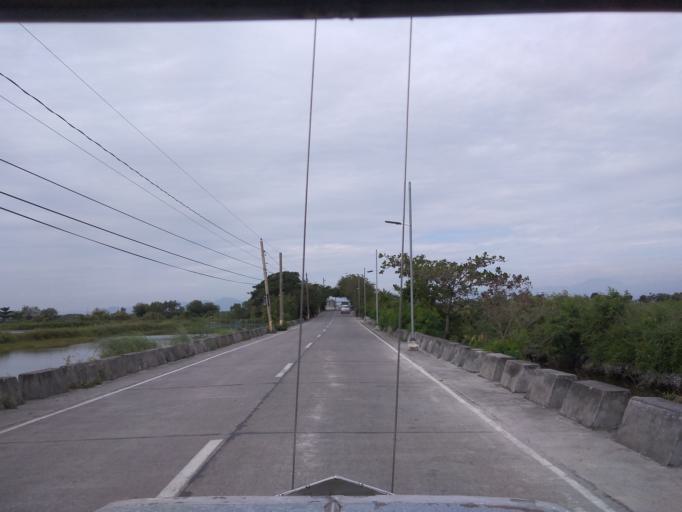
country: PH
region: Central Luzon
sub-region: Province of Pampanga
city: Sexmoan
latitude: 14.9373
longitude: 120.6158
